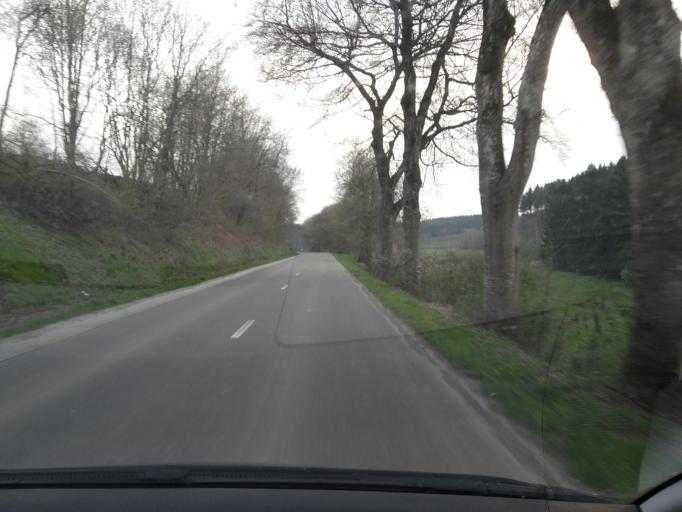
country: BE
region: Wallonia
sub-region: Province du Luxembourg
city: Bertrix
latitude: 49.8413
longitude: 5.2500
